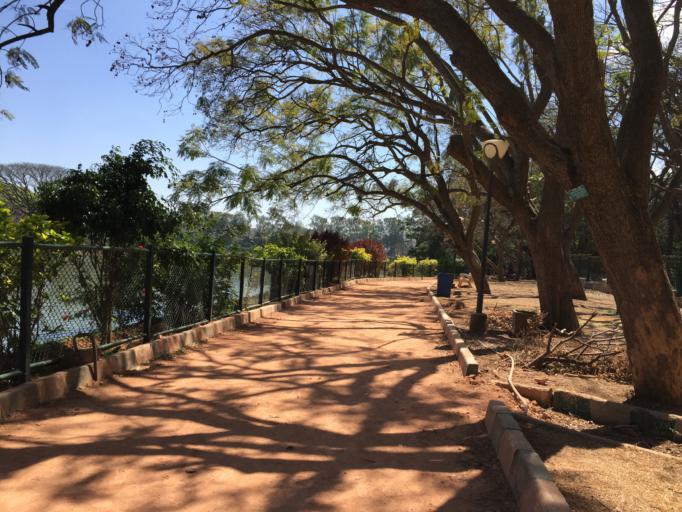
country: IN
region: Karnataka
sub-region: Bangalore Urban
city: Bangalore
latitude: 12.9472
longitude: 77.5818
